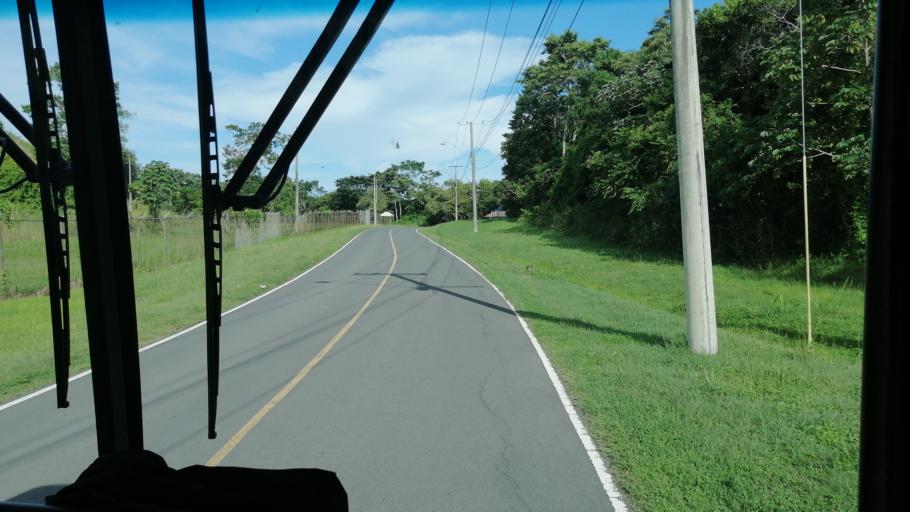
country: PA
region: Panama
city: Veracruz
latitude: 8.9010
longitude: -79.5852
